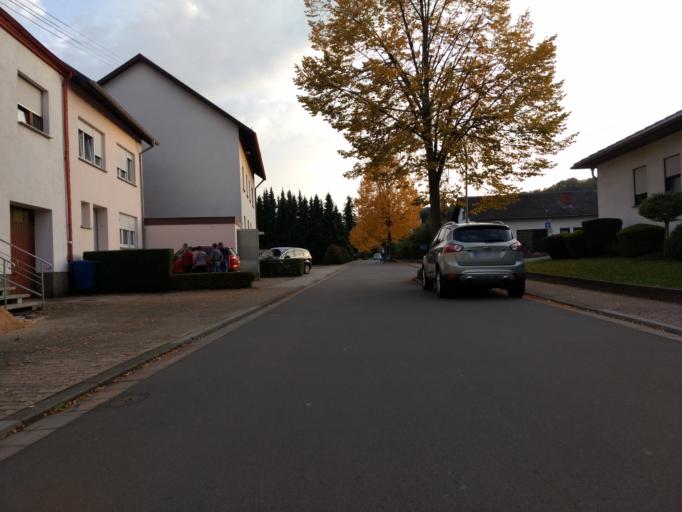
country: DE
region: Saarland
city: Rehlingen-Siersburg
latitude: 49.3773
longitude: 6.6779
